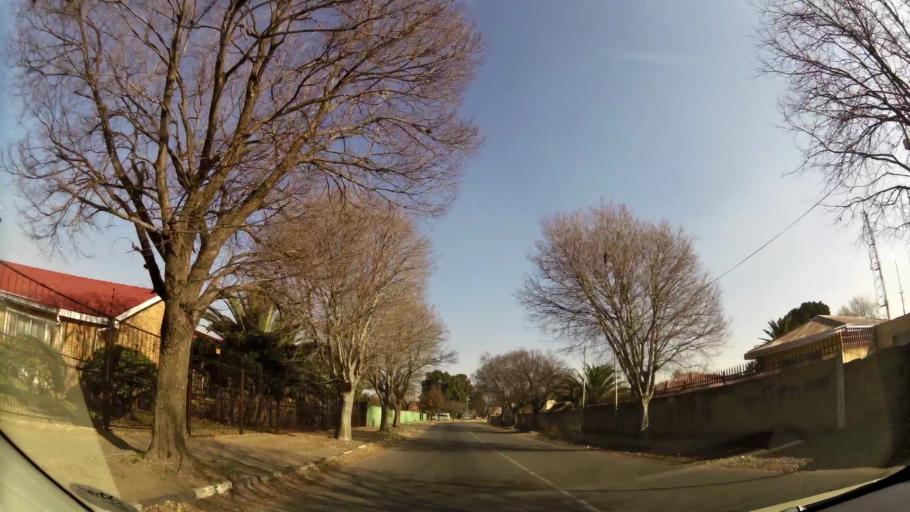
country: ZA
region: Gauteng
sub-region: West Rand District Municipality
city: Randfontein
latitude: -26.1770
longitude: 27.7071
